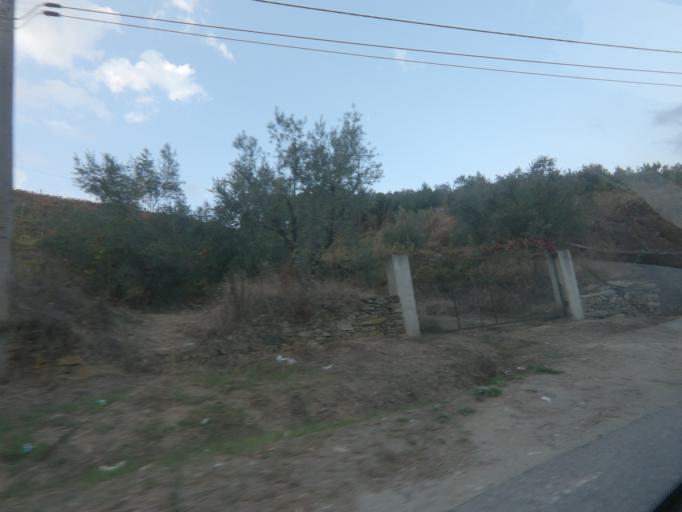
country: PT
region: Vila Real
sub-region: Mesao Frio
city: Mesao Frio
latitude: 41.1813
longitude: -7.8577
